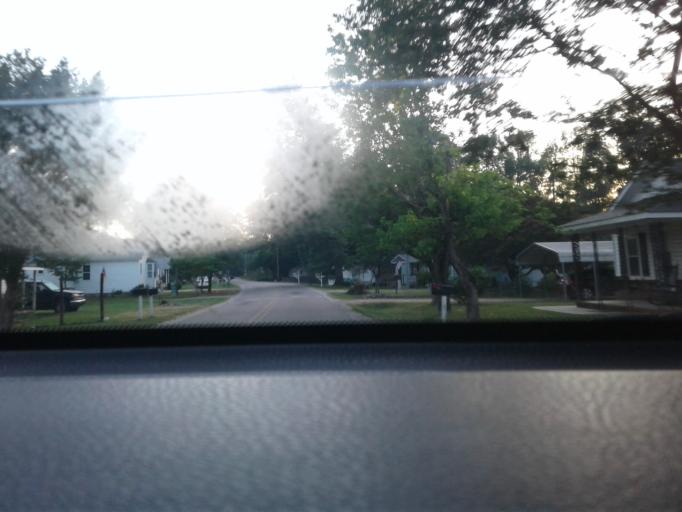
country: US
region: North Carolina
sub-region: Harnett County
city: Erwin
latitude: 35.3220
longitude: -78.6528
